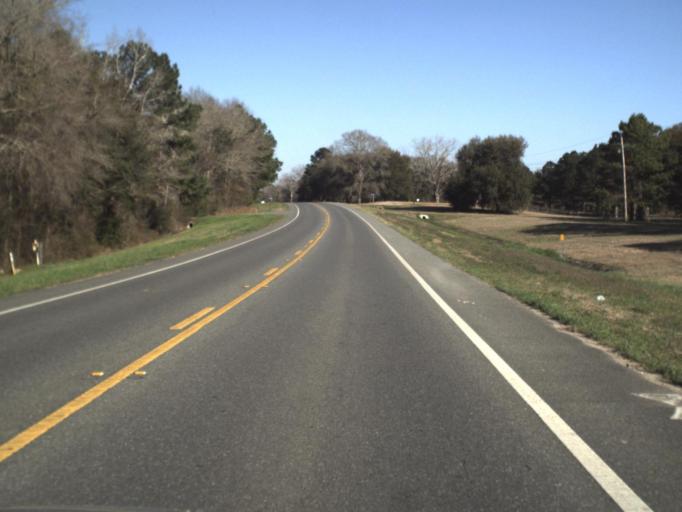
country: US
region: Florida
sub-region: Jackson County
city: Marianna
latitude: 30.7854
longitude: -85.3432
